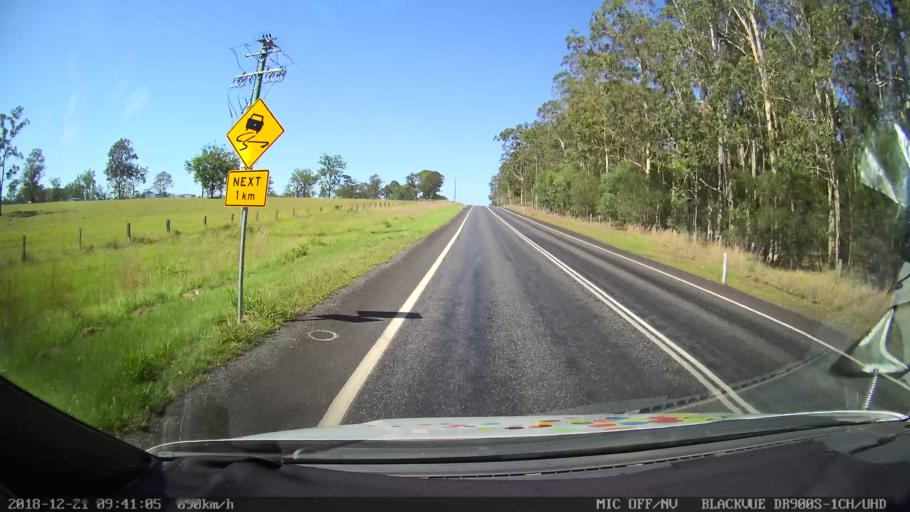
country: AU
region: New South Wales
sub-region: Clarence Valley
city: Grafton
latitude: -29.5811
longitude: 152.9606
